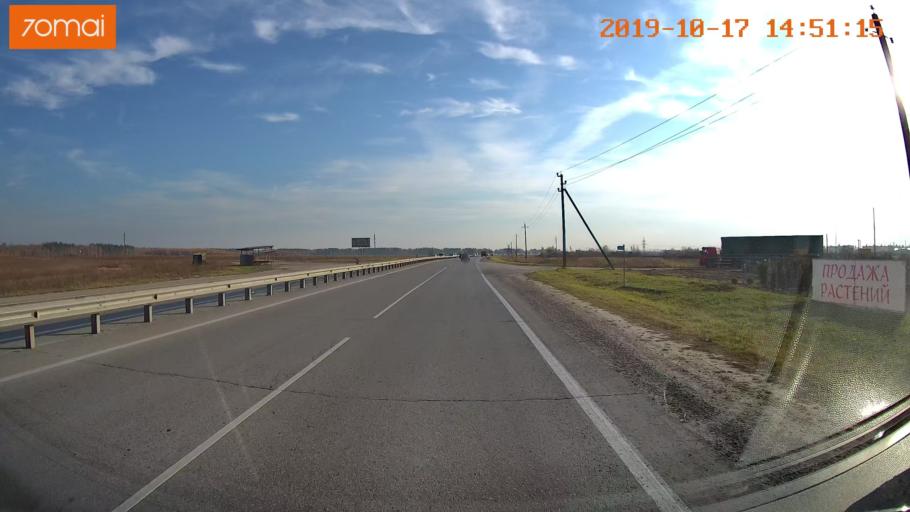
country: RU
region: Rjazan
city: Polyany
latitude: 54.7222
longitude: 39.8470
